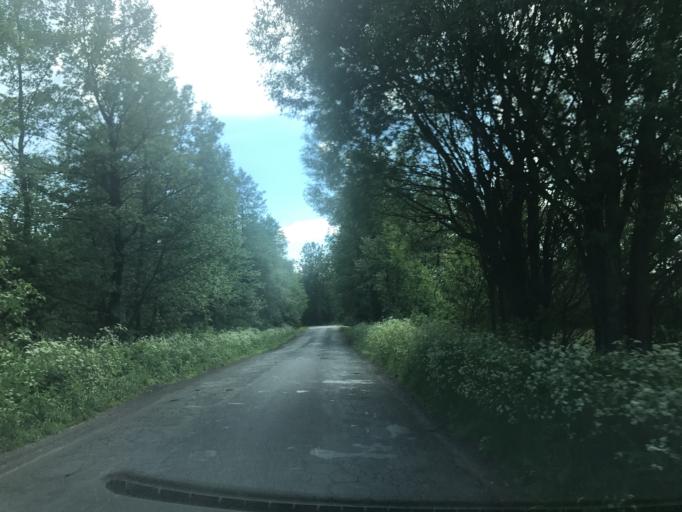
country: PL
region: Warmian-Masurian Voivodeship
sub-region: Powiat ilawski
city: Lubawa
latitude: 53.3969
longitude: 19.7400
